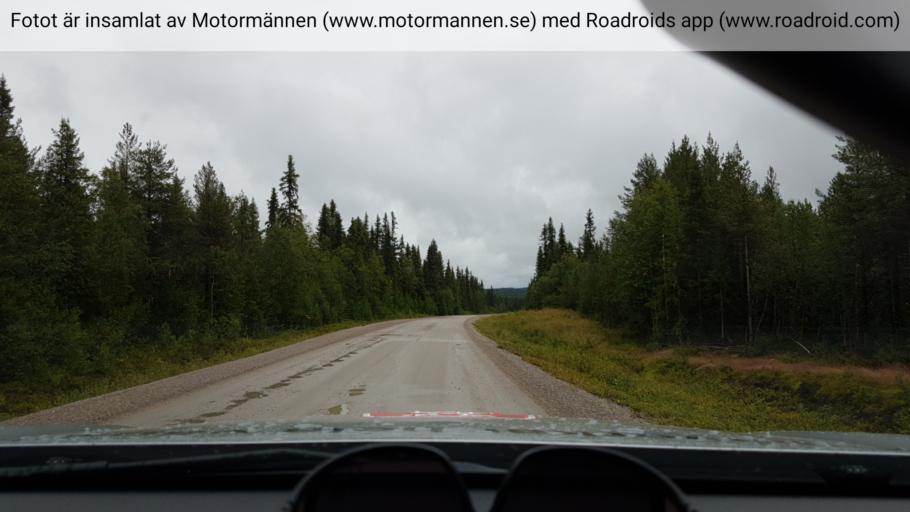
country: SE
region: Vaesterbotten
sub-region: Storumans Kommun
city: Storuman
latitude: 64.8840
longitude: 17.3110
